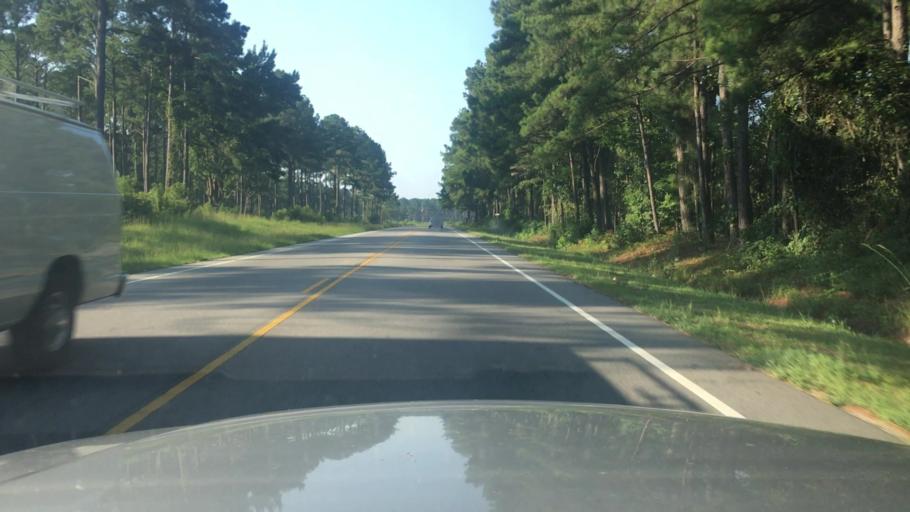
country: US
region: North Carolina
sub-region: Harnett County
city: Walkertown
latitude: 35.1982
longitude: -78.8495
